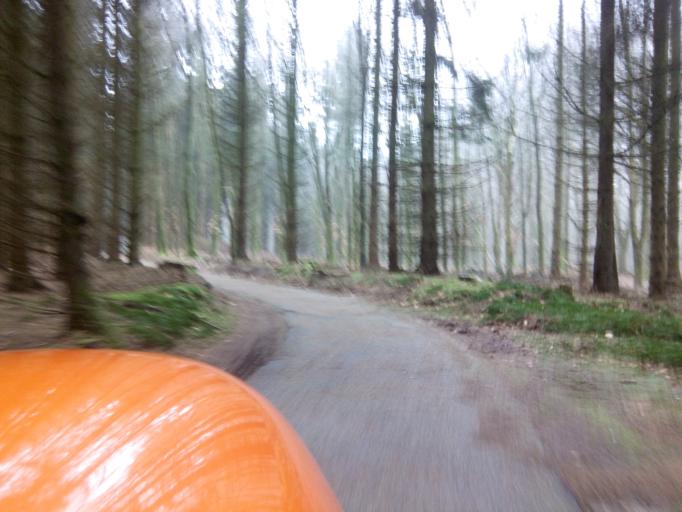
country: NL
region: Gelderland
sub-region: Gemeente Barneveld
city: Garderen
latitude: 52.2509
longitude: 5.6968
